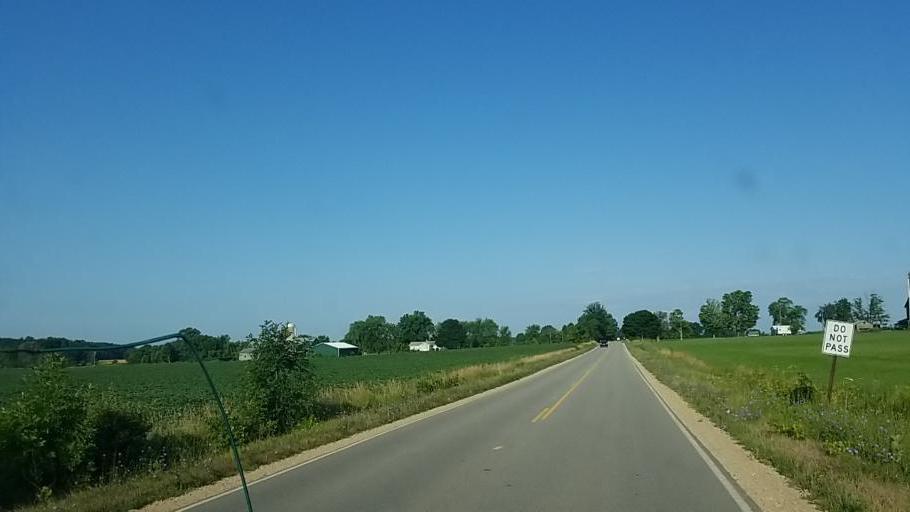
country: US
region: Michigan
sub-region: Newaygo County
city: Newaygo
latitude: 43.3511
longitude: -85.8457
